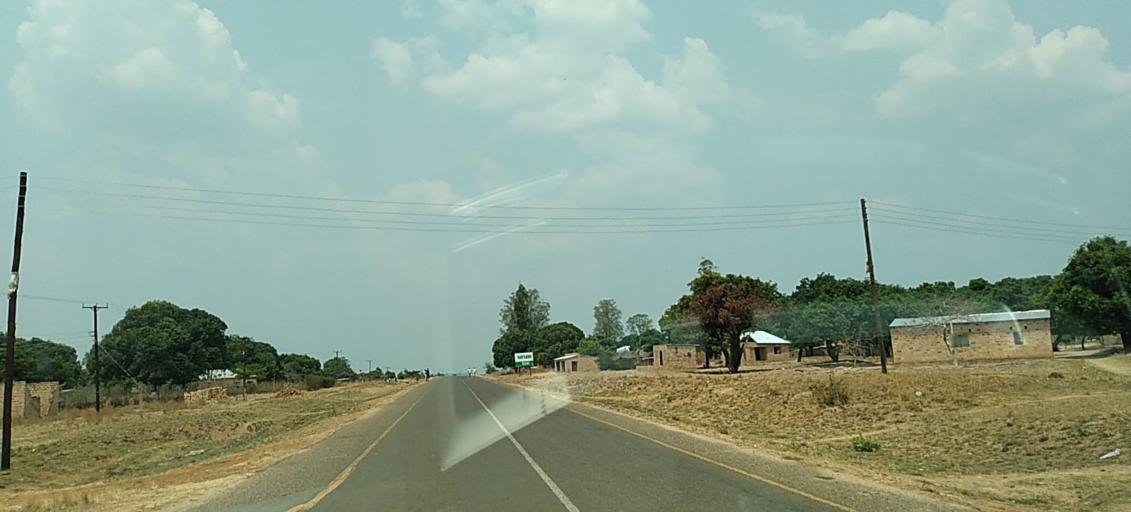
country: ZM
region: North-Western
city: Zambezi
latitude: -13.5506
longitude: 23.1145
